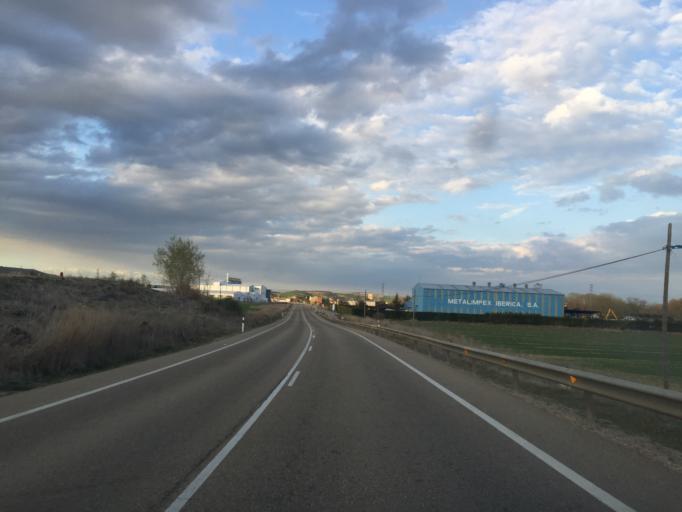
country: ES
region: Castille and Leon
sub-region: Provincia de Palencia
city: Soto de Cerrato
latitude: 41.9740
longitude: -4.4377
